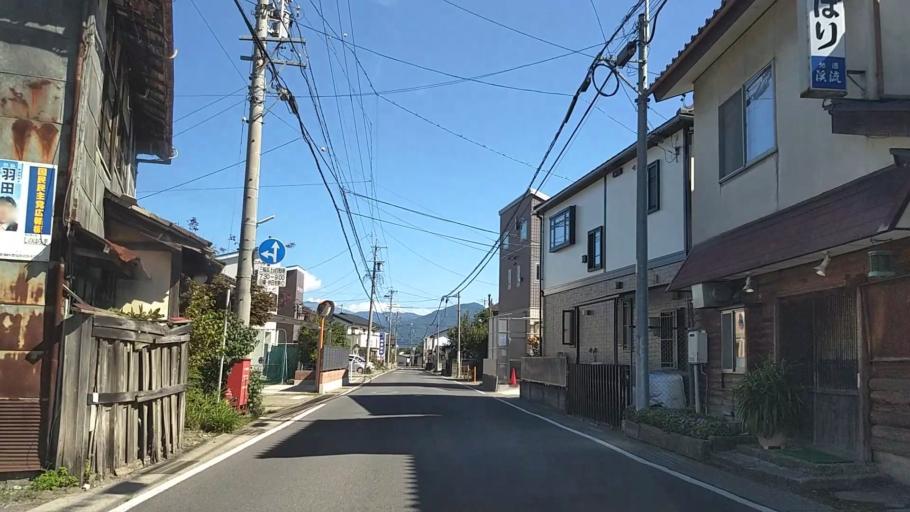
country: JP
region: Nagano
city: Nagano-shi
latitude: 36.6115
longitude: 138.1588
